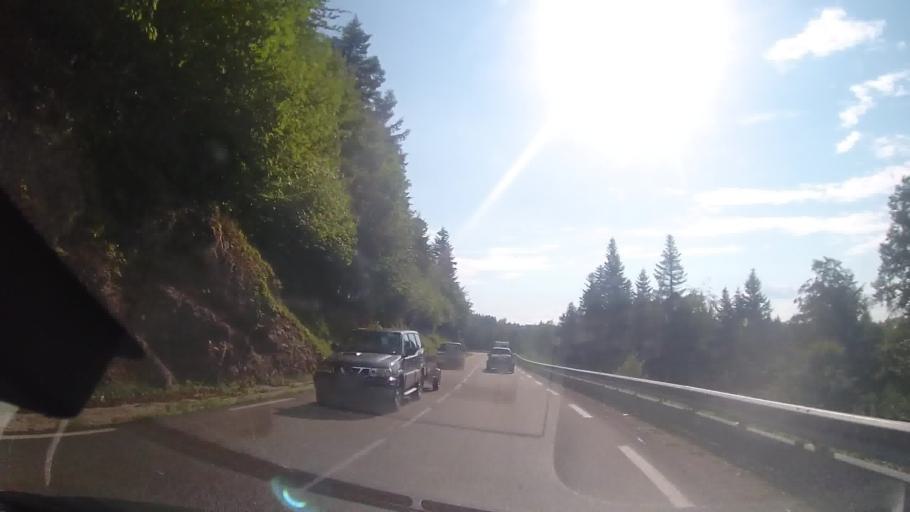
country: FR
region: Franche-Comte
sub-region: Departement du Jura
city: Champagnole
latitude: 46.6114
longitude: 5.8907
